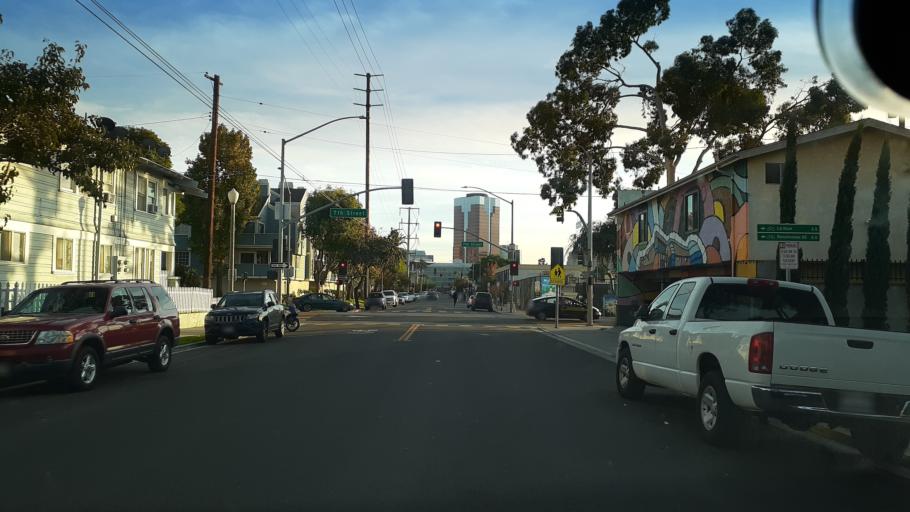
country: US
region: California
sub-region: Los Angeles County
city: Long Beach
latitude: 33.7758
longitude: -118.1994
